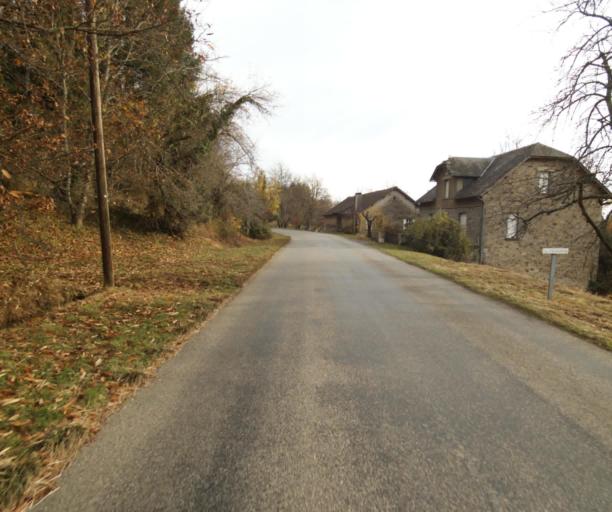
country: FR
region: Limousin
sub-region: Departement de la Correze
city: Sainte-Fortunade
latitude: 45.1954
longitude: 1.7751
